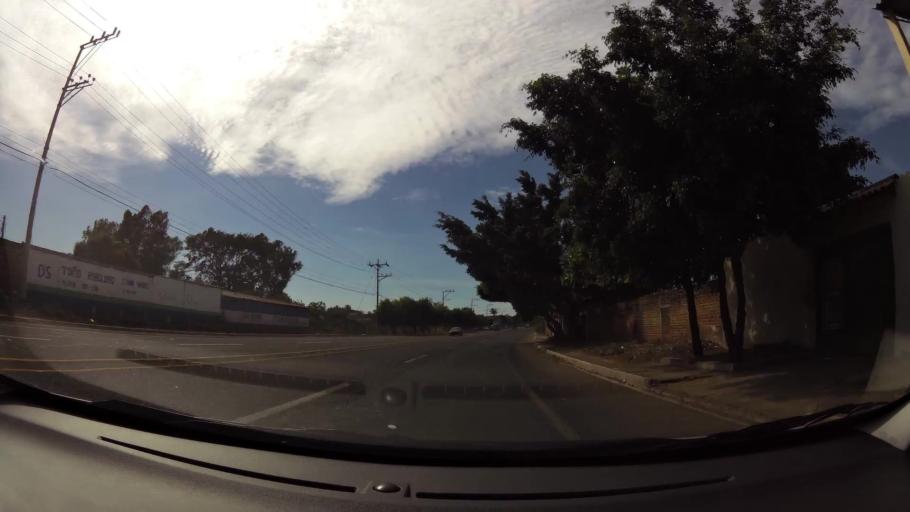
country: SV
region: Santa Ana
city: Chalchuapa
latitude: 13.9877
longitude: -89.6845
